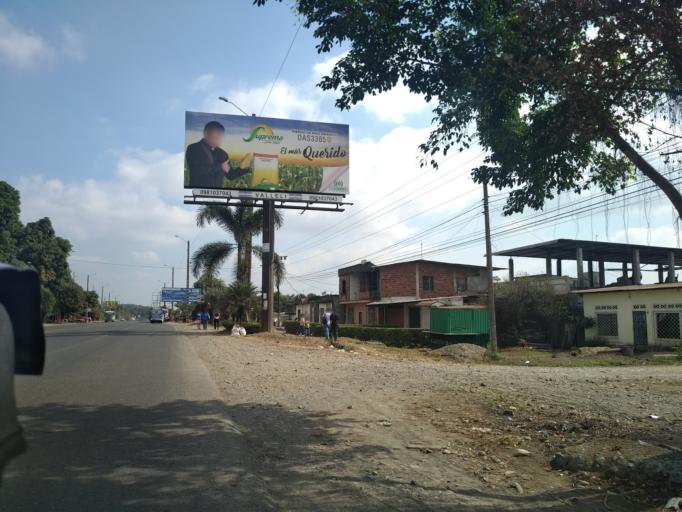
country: EC
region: Los Rios
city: Quevedo
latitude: -1.0594
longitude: -79.4890
